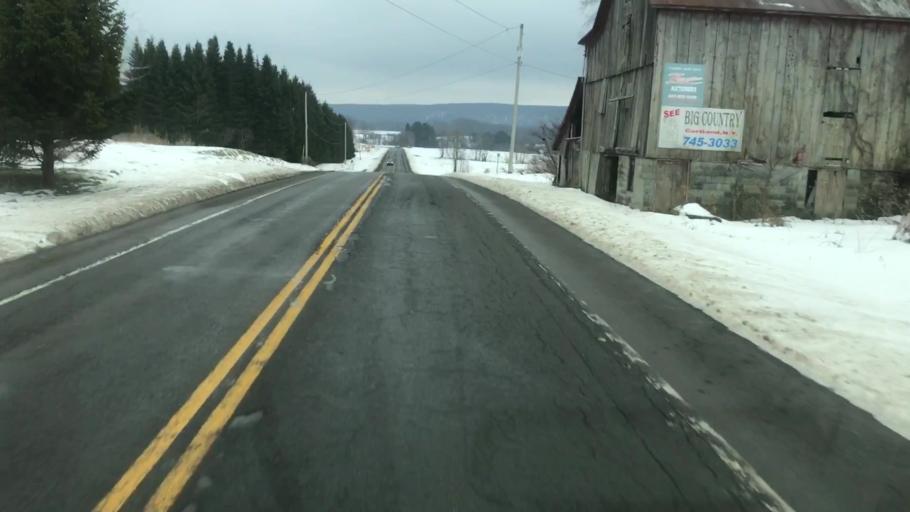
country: US
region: New York
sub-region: Cayuga County
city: Moravia
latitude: 42.7106
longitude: -76.3124
